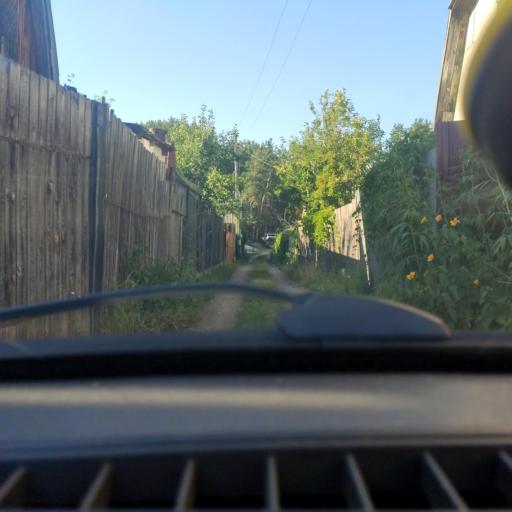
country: RU
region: Samara
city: Zhigulevsk
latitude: 53.5015
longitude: 49.5037
